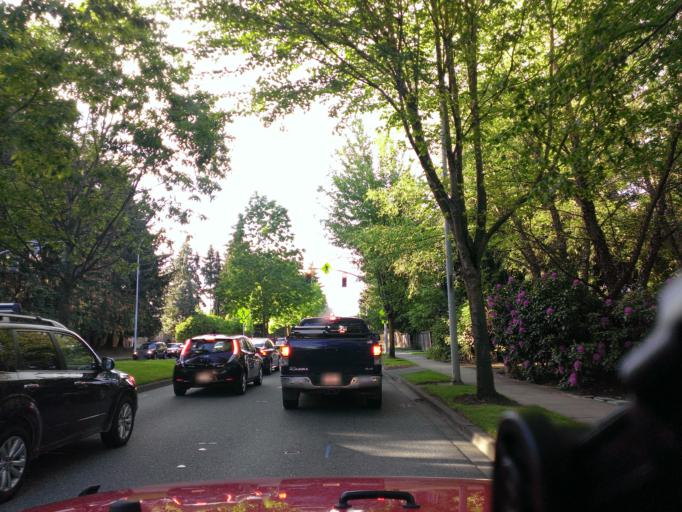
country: US
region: Washington
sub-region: King County
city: Redmond
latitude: 47.6603
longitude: -122.1432
